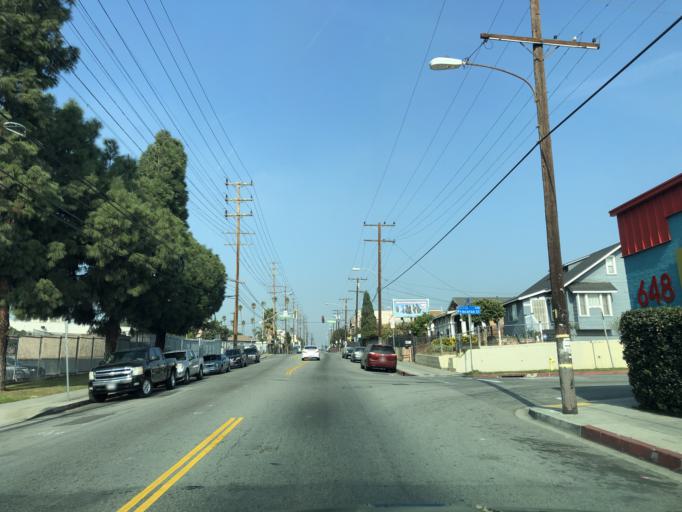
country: US
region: California
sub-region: Los Angeles County
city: Boyle Heights
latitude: 34.0270
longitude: -118.1923
